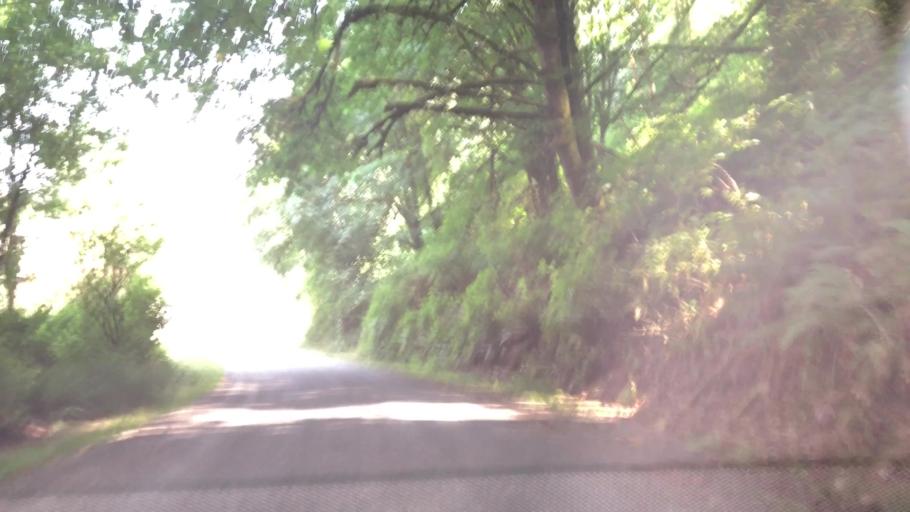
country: US
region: Washington
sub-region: Snohomish County
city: Lochsloy
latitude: 48.0509
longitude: -122.0214
